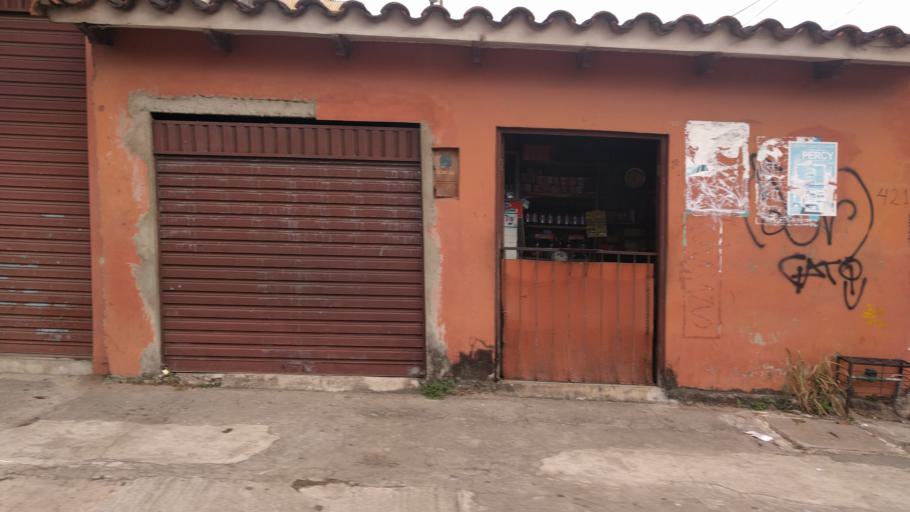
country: BO
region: Santa Cruz
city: Santa Cruz de la Sierra
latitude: -17.7777
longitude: -63.2094
